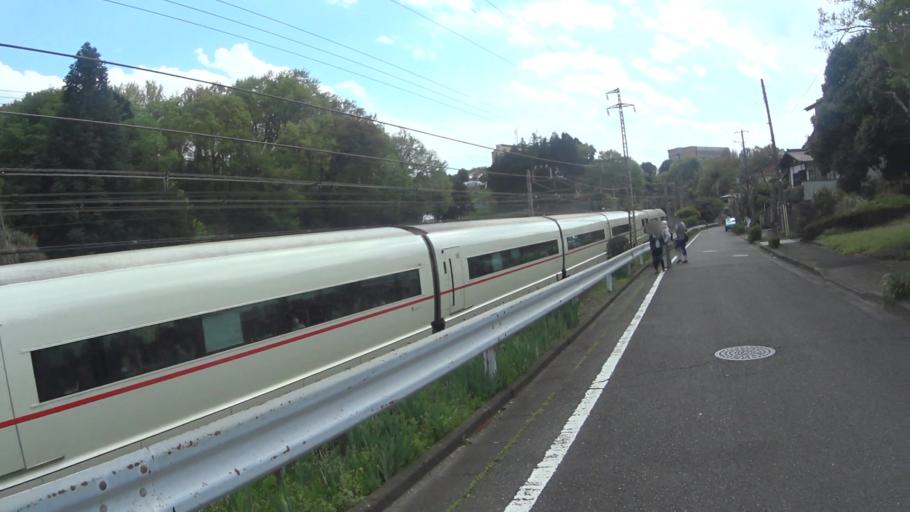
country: JP
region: Tokyo
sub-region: Machida-shi
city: Machida
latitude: 35.5736
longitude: 139.4714
